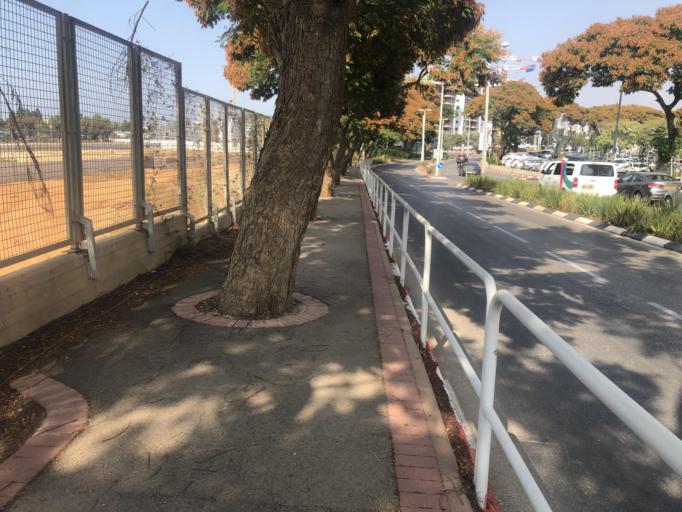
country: IL
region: Tel Aviv
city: Or Yehuda
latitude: 32.0467
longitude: 34.8409
